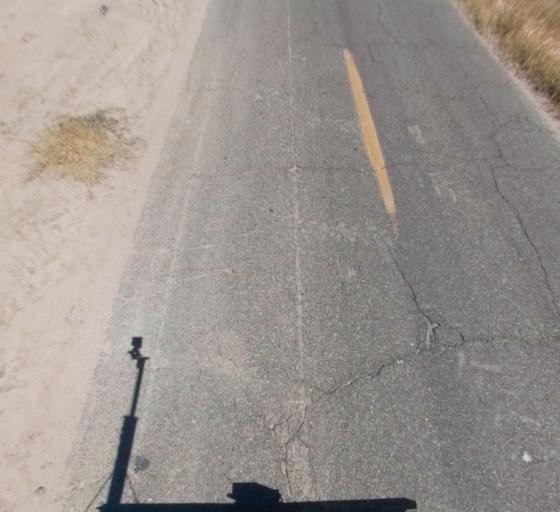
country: US
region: California
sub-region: Fresno County
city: Biola
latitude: 36.8444
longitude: -120.0010
